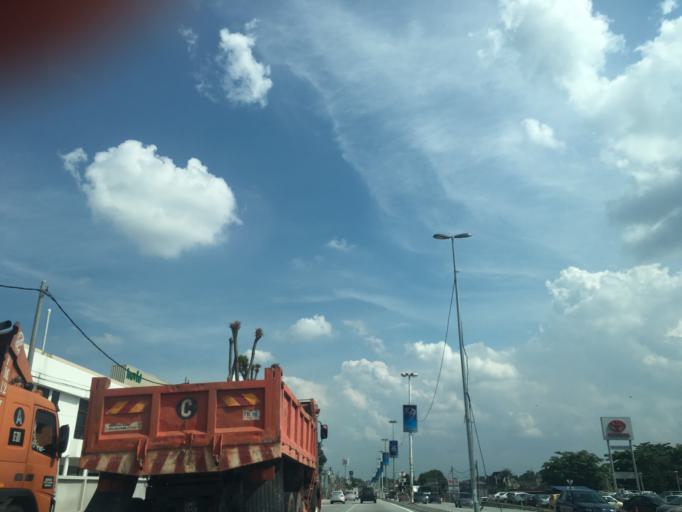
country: MY
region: Perak
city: Ipoh
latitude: 4.6283
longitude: 101.0824
